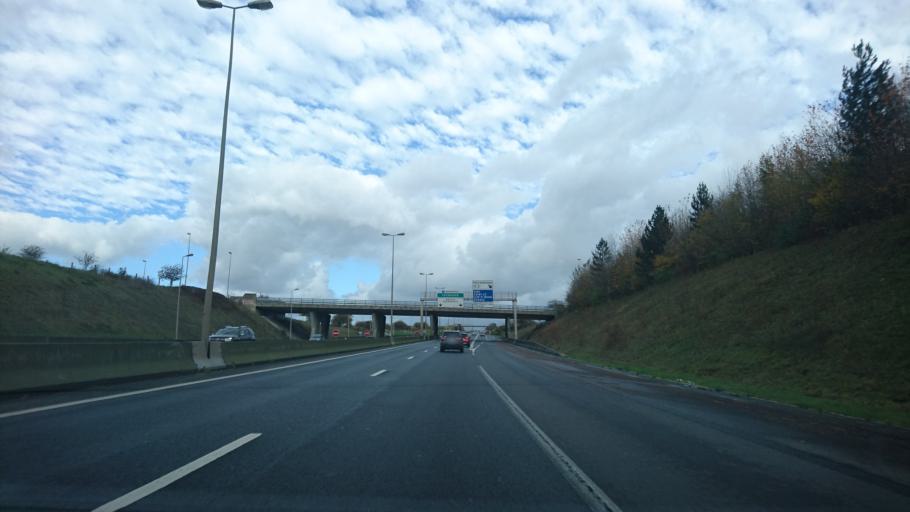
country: FR
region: Lower Normandy
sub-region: Departement du Calvados
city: Bretteville-sur-Odon
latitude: 49.1612
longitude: -0.4274
